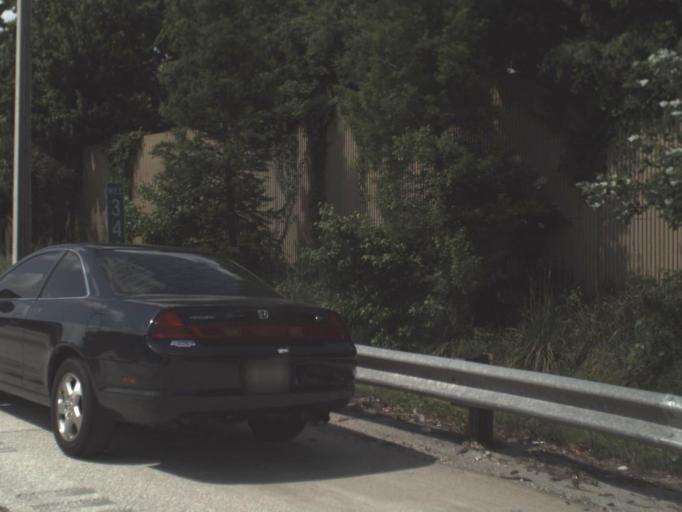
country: US
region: Florida
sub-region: Duval County
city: Jacksonville
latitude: 30.2773
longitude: -81.6176
